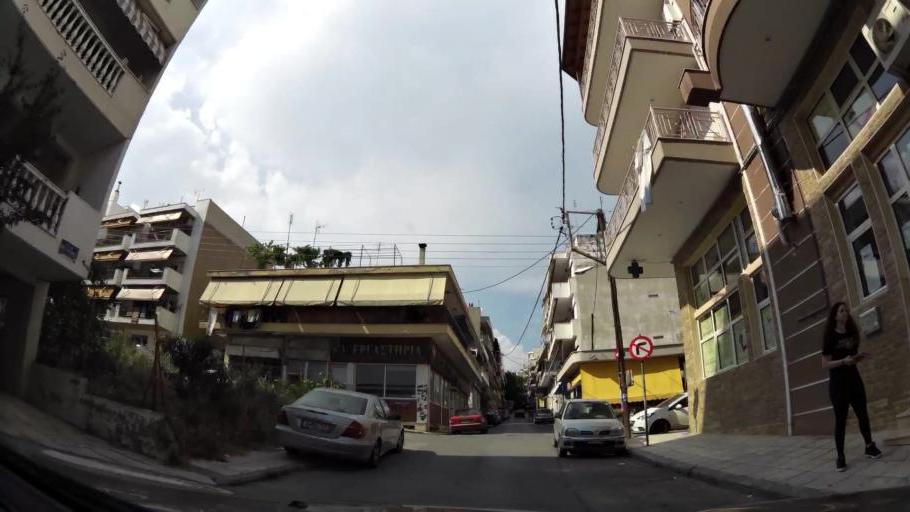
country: GR
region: Central Macedonia
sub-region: Nomos Thessalonikis
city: Polichni
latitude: 40.6614
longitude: 22.9439
